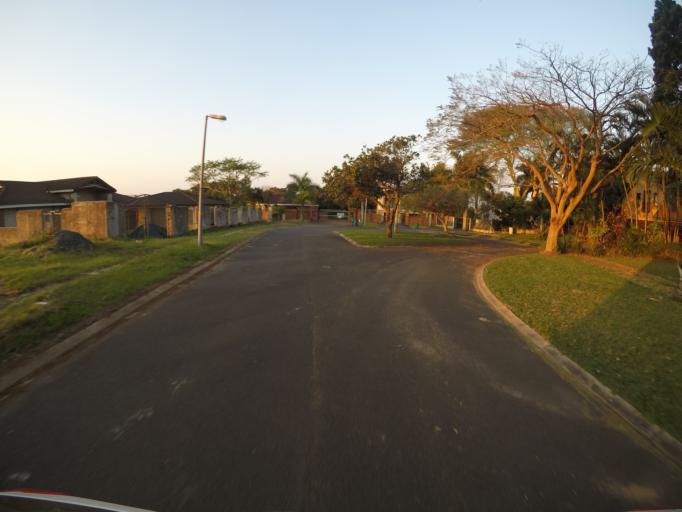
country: ZA
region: KwaZulu-Natal
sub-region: uThungulu District Municipality
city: Richards Bay
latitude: -28.7630
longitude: 32.1203
